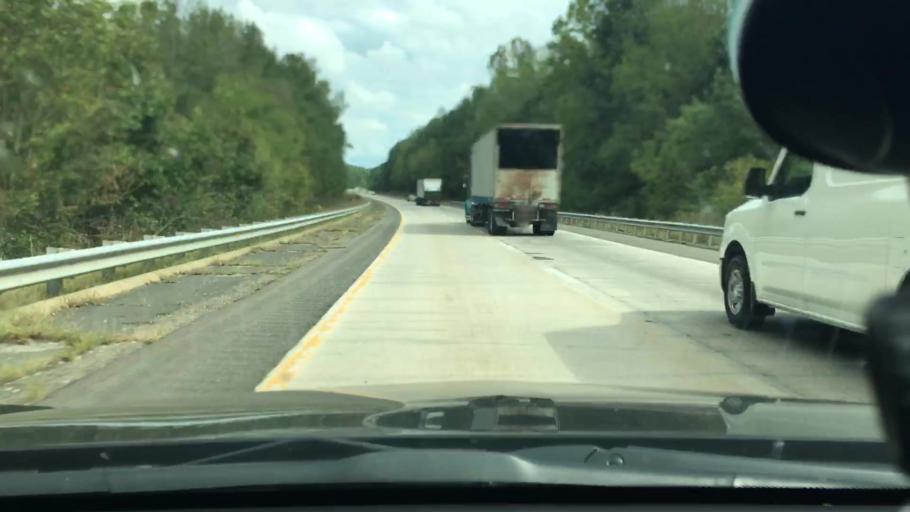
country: US
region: North Carolina
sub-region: Davie County
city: Mocksville
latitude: 35.8920
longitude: -80.6551
